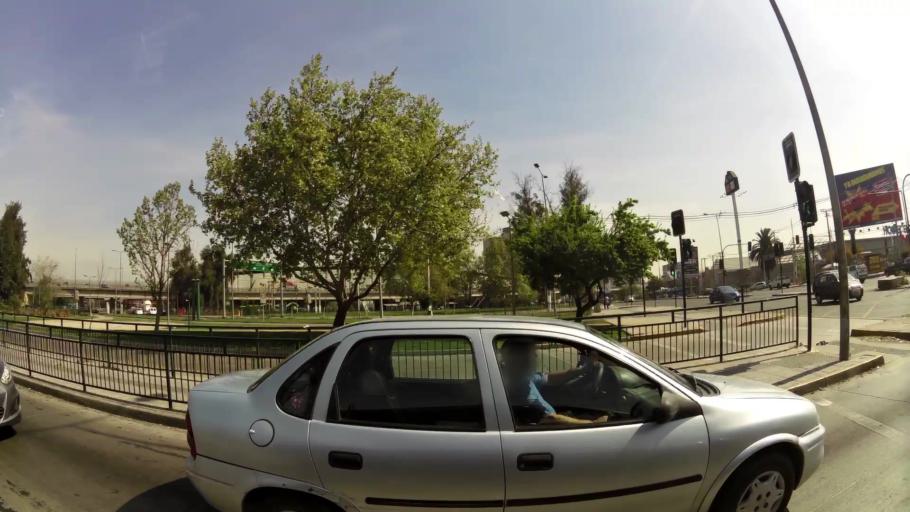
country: CL
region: Santiago Metropolitan
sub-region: Provincia de Santiago
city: Villa Presidente Frei, Nunoa, Santiago, Chile
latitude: -33.5105
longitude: -70.5884
